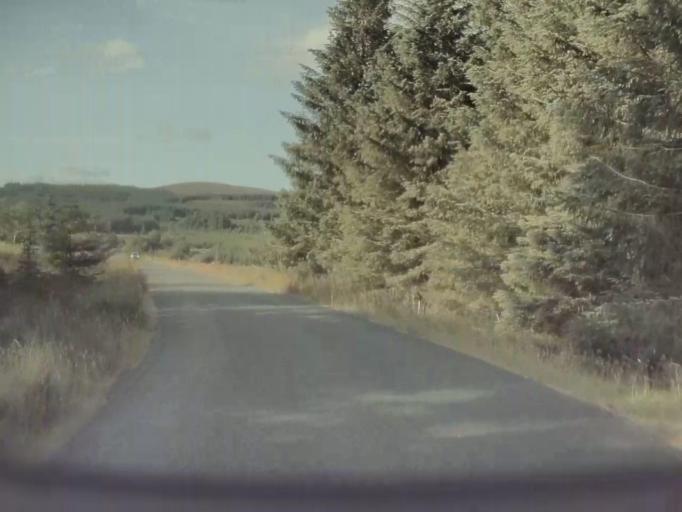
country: IE
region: Leinster
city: Oldbawn
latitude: 53.0911
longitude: -6.3480
